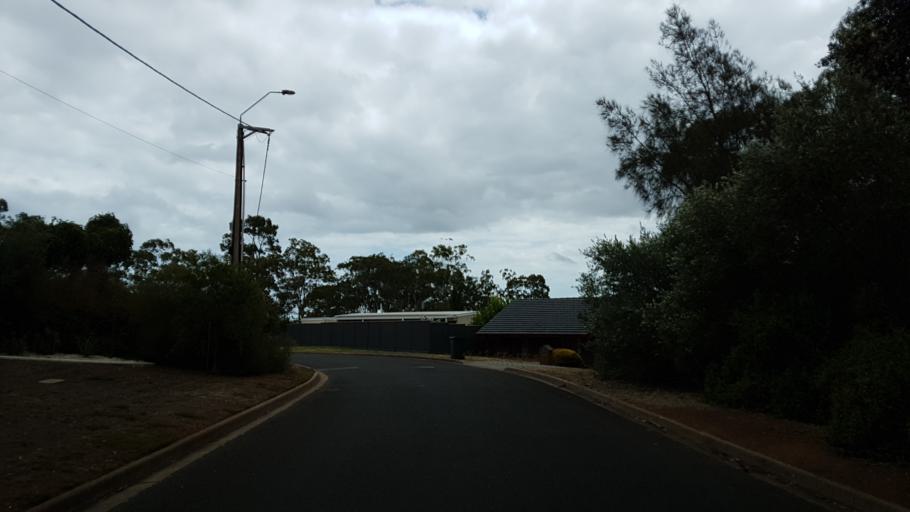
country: AU
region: South Australia
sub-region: Mitcham
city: Clapham
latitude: -35.0047
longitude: 138.5946
